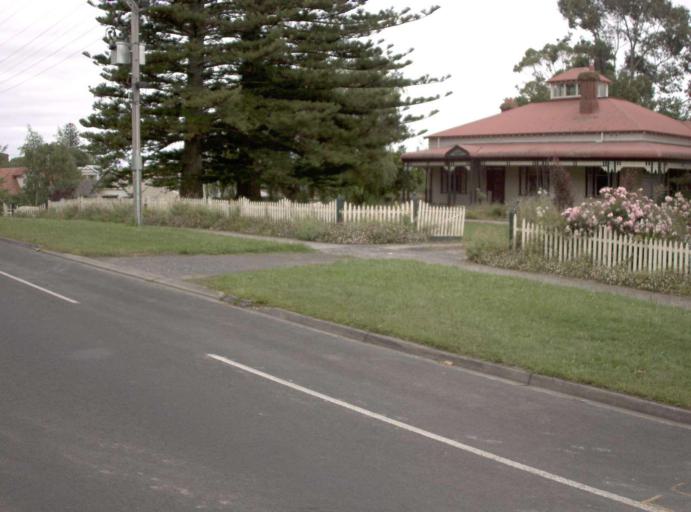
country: AU
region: Victoria
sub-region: Bass Coast
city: North Wonthaggi
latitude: -38.4348
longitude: 145.8191
